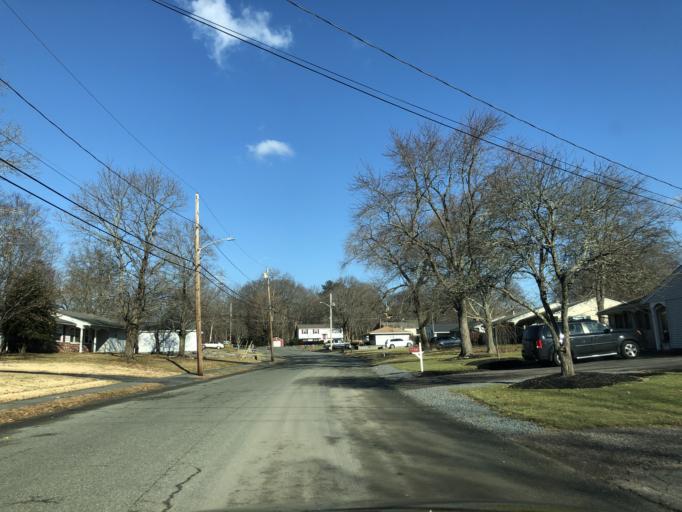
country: US
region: Massachusetts
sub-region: Plymouth County
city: Brockton
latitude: 42.1059
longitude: -71.0002
